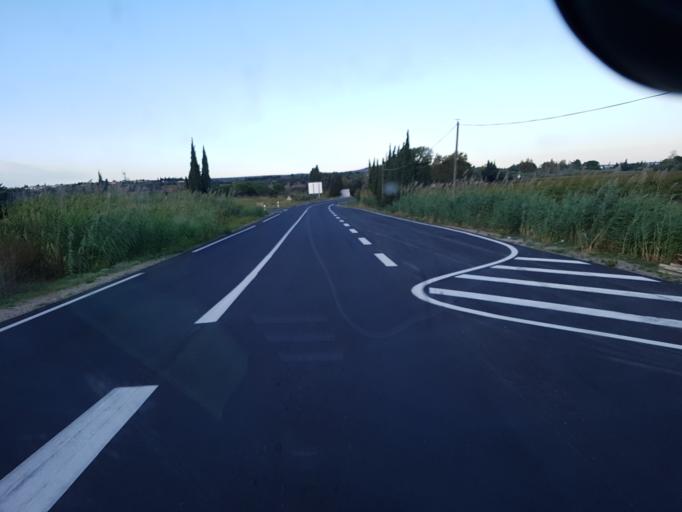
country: FR
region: Languedoc-Roussillon
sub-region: Departement de l'Aude
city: Leucate
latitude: 42.9593
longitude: 2.9857
